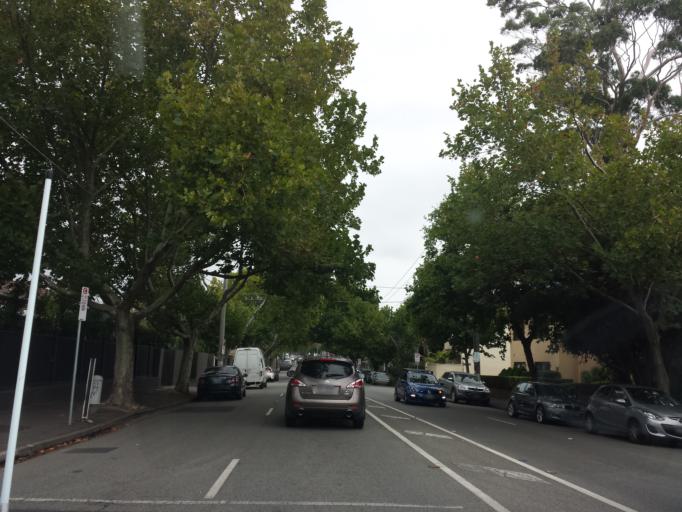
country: AU
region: Victoria
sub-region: Stonnington
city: Toorak
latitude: -37.8462
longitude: 145.0036
